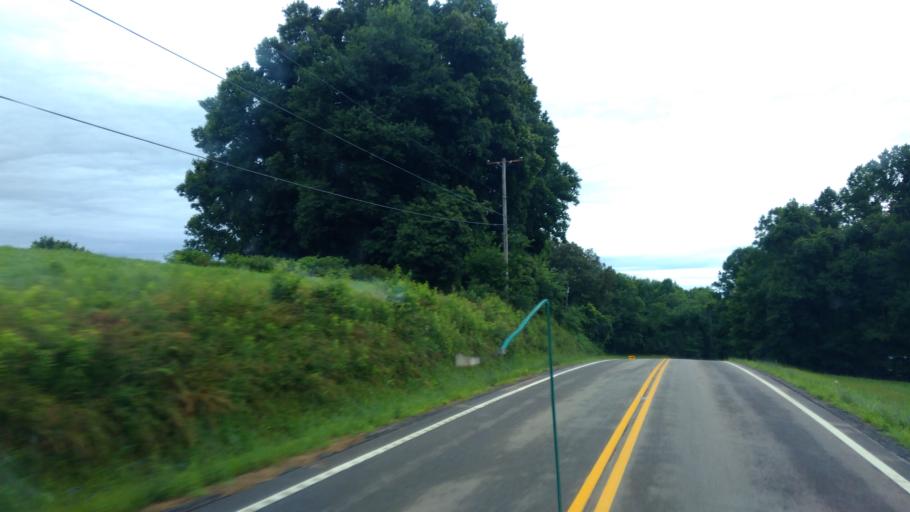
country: US
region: Ohio
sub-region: Stark County
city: Minerva
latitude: 40.6944
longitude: -81.0129
